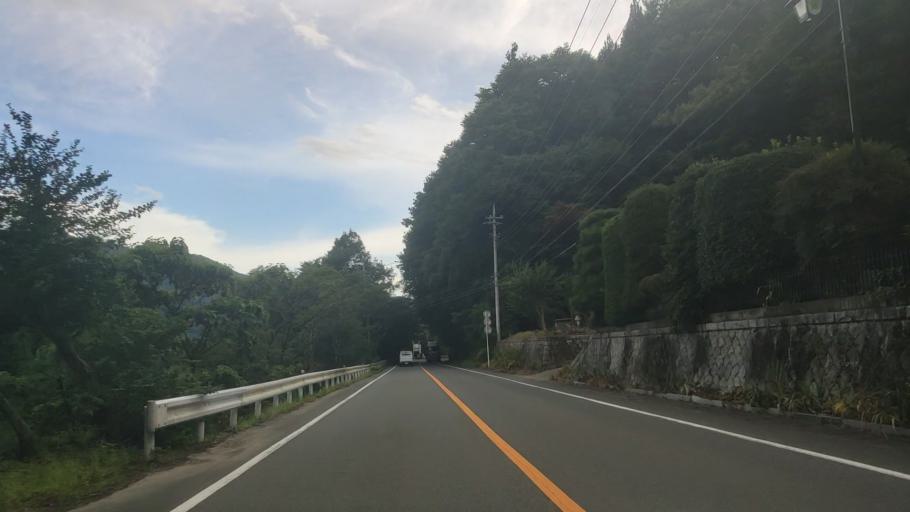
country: JP
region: Gunma
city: Omamacho-omama
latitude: 36.5237
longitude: 139.3086
